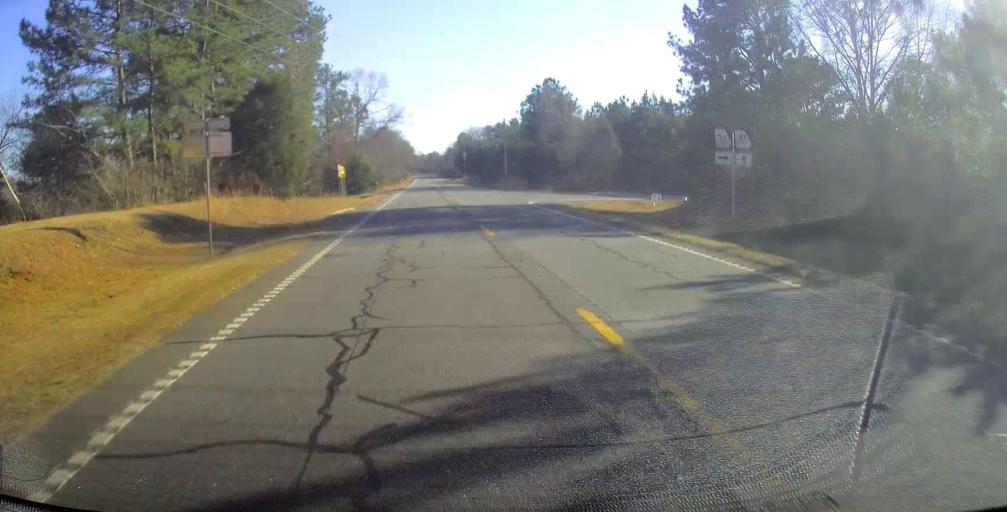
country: US
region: Georgia
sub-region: Talbot County
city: Talbotton
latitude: 32.7624
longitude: -84.5580
